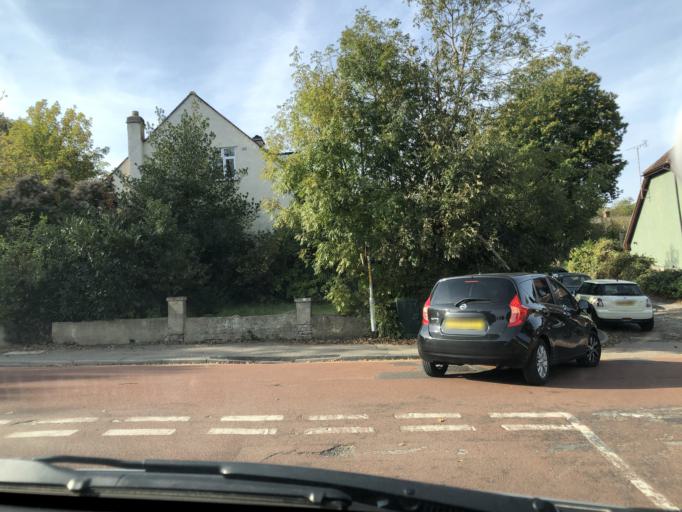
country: GB
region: England
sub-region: Greater London
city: Bexley
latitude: 51.4270
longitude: 0.1676
